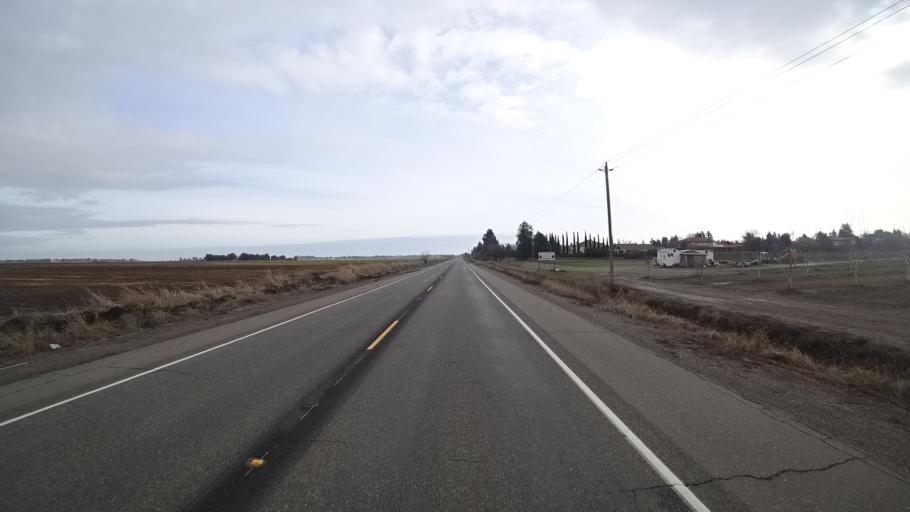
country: US
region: California
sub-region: Yolo County
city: Davis
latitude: 38.5614
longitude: -121.7956
